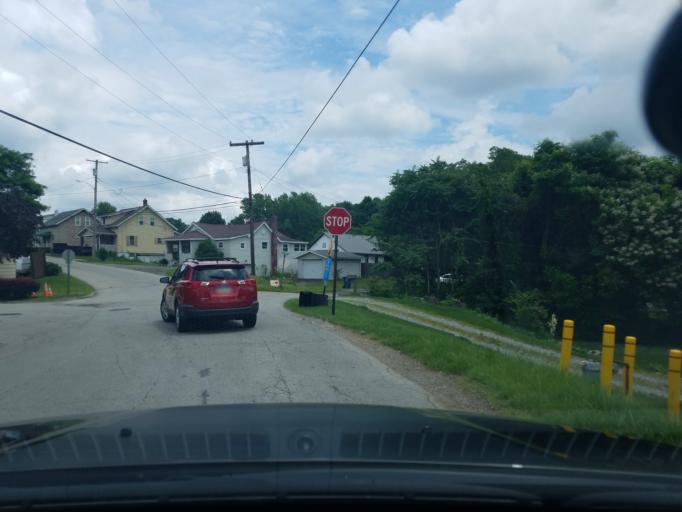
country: US
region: Pennsylvania
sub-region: Westmoreland County
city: Youngwood
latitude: 40.2291
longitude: -79.5864
